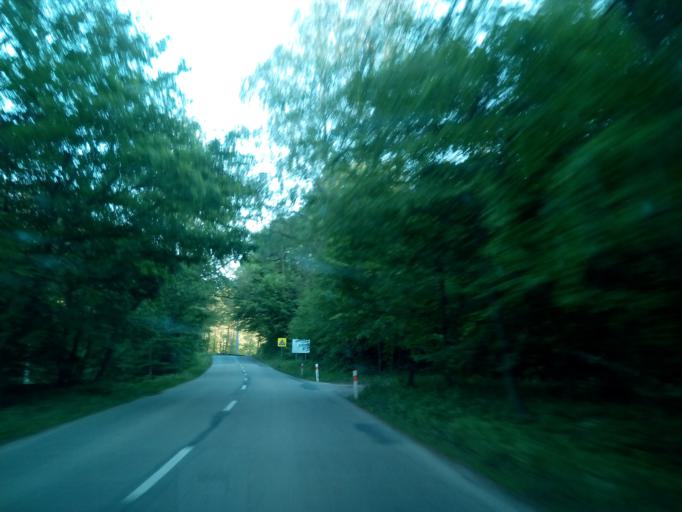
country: CZ
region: South Moravian
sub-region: Okres Blansko
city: Jedovnice
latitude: 49.3058
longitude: 16.7445
